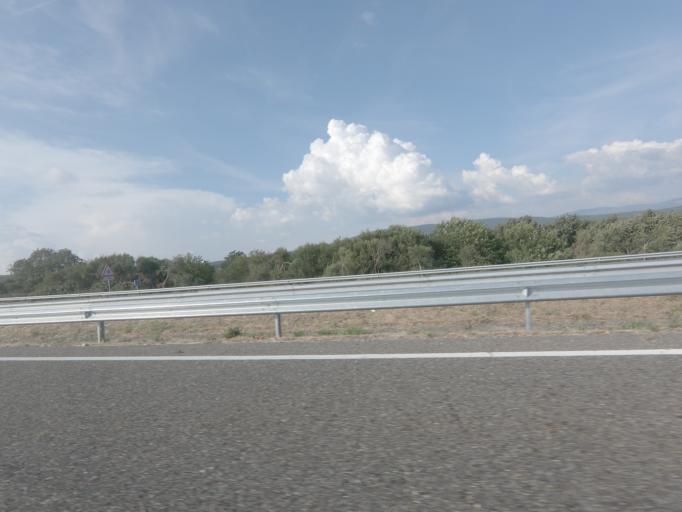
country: ES
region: Galicia
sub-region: Provincia de Ourense
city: Cualedro
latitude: 41.9839
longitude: -7.5473
